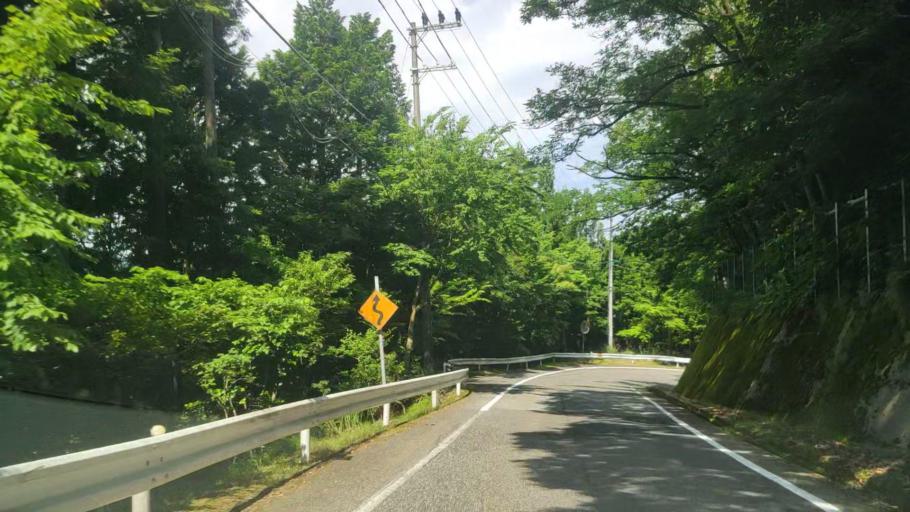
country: JP
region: Hyogo
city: Toyooka
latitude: 35.6382
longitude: 134.7731
